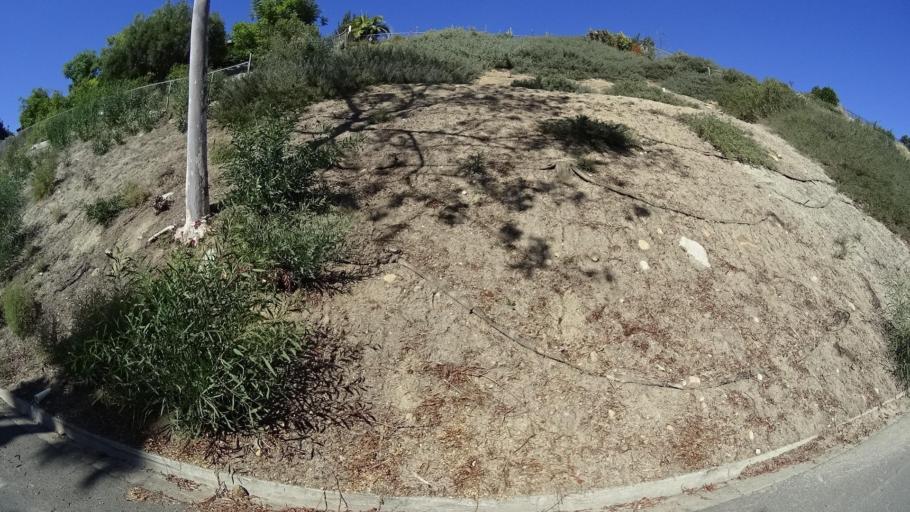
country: US
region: California
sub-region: San Diego County
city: Casa de Oro-Mount Helix
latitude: 32.7557
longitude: -116.9817
